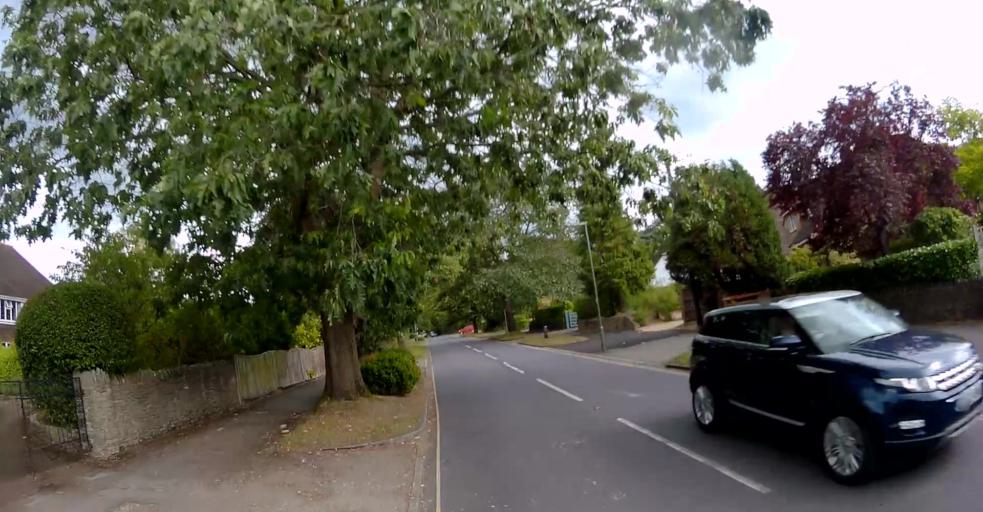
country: GB
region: England
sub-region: Surrey
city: Farnham
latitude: 51.2113
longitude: -0.7853
